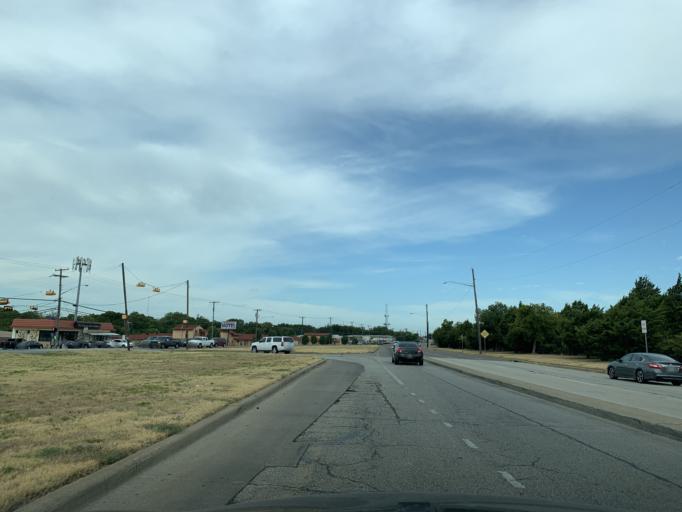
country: US
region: Texas
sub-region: Dallas County
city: Cockrell Hill
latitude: 32.7500
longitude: -96.8800
